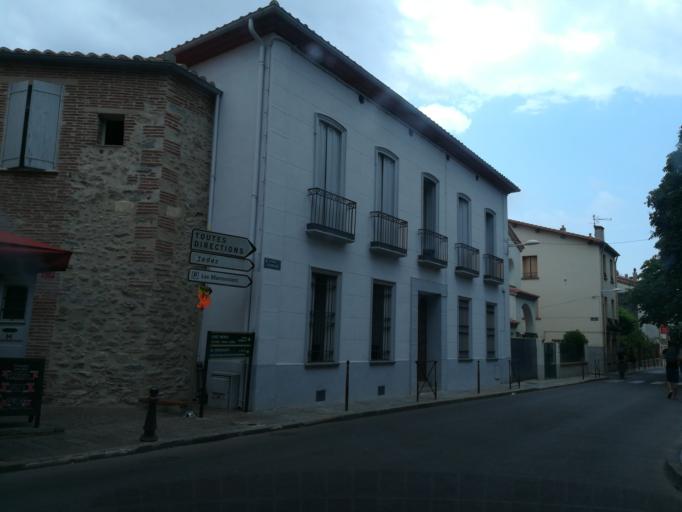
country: FR
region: Languedoc-Roussillon
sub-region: Departement des Pyrenees-Orientales
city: Ceret
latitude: 42.4852
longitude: 2.7498
